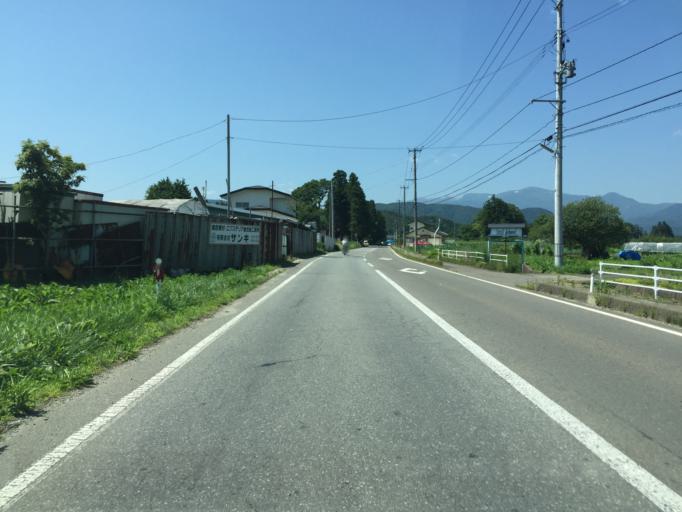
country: JP
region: Fukushima
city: Fukushima-shi
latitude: 37.7227
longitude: 140.4025
